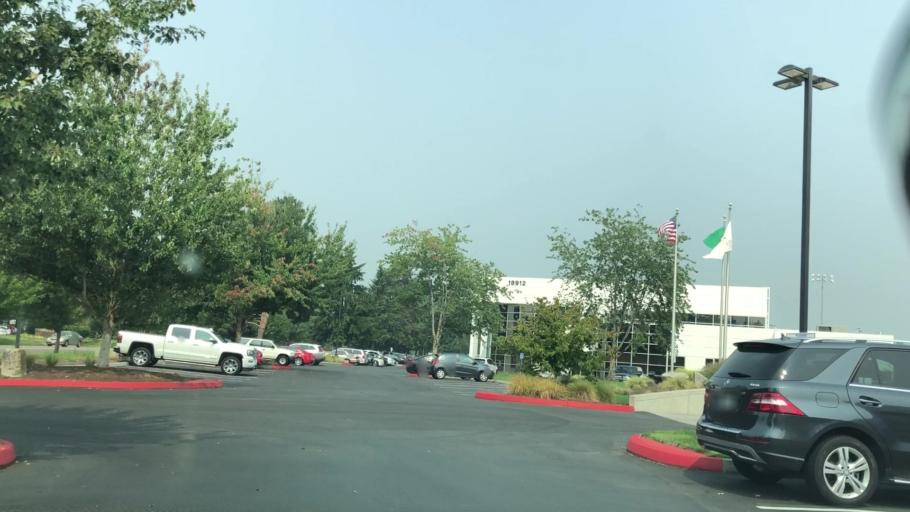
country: US
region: Washington
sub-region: King County
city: Woodinville
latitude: 47.7638
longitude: -122.1828
